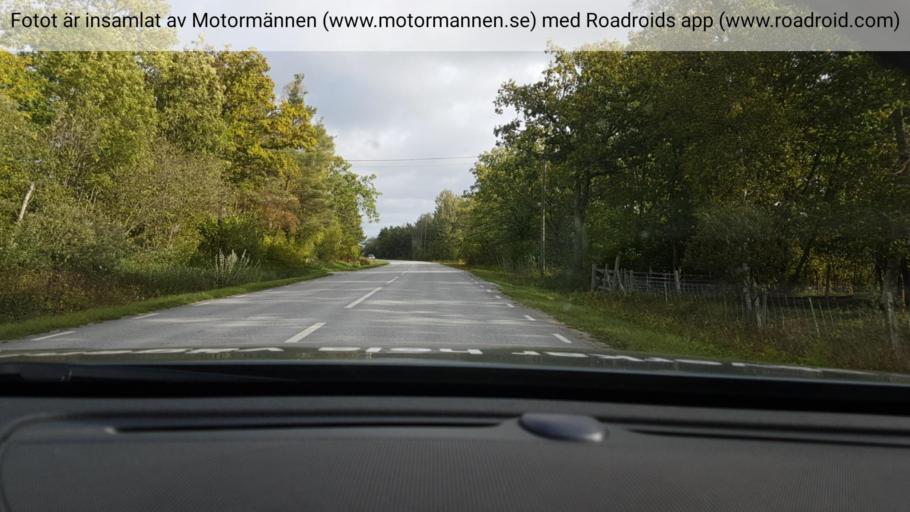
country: SE
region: Gotland
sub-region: Gotland
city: Slite
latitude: 57.7691
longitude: 18.7723
